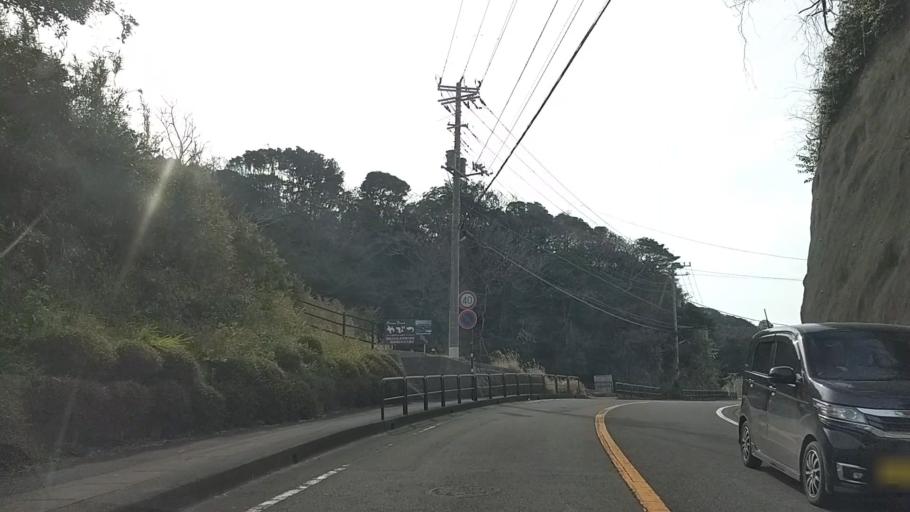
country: JP
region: Shizuoka
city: Shimoda
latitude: 34.6726
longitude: 138.9644
